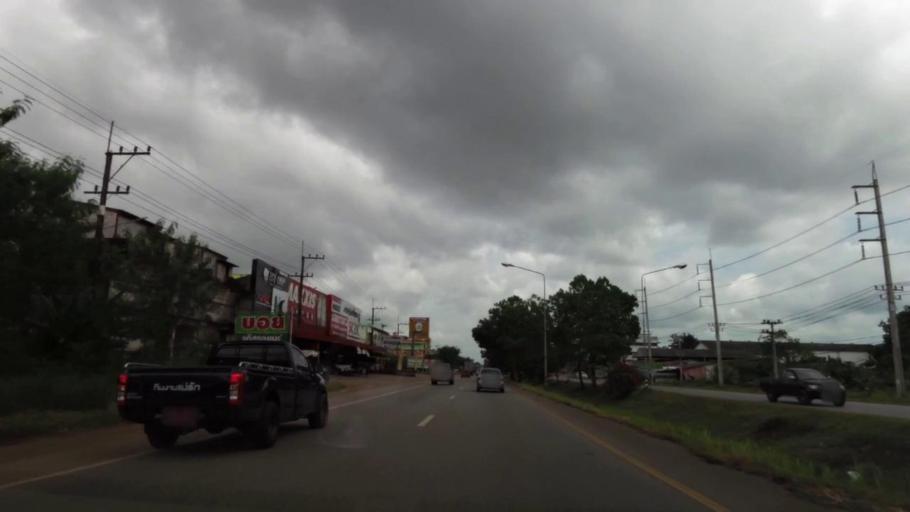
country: TH
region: Chanthaburi
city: Na Yai Am
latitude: 12.7806
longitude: 101.8184
